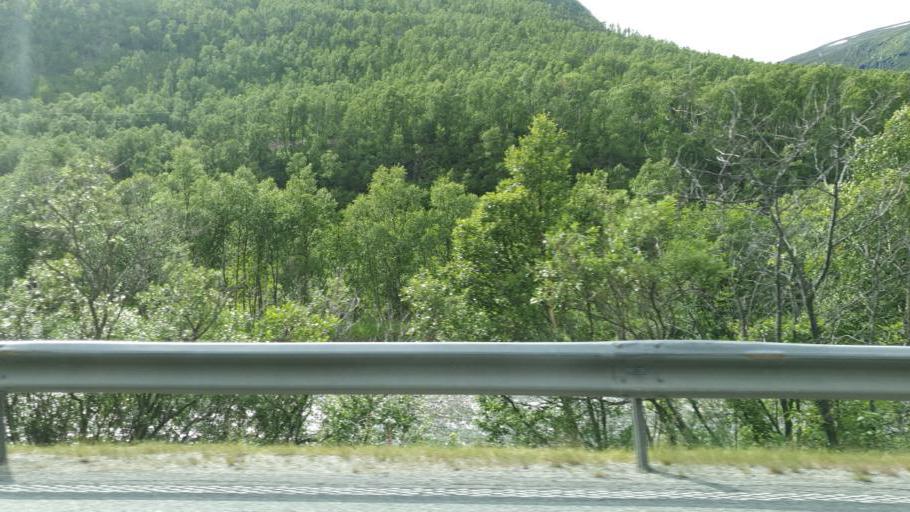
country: NO
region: Sor-Trondelag
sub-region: Oppdal
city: Oppdal
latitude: 62.3722
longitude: 9.6381
